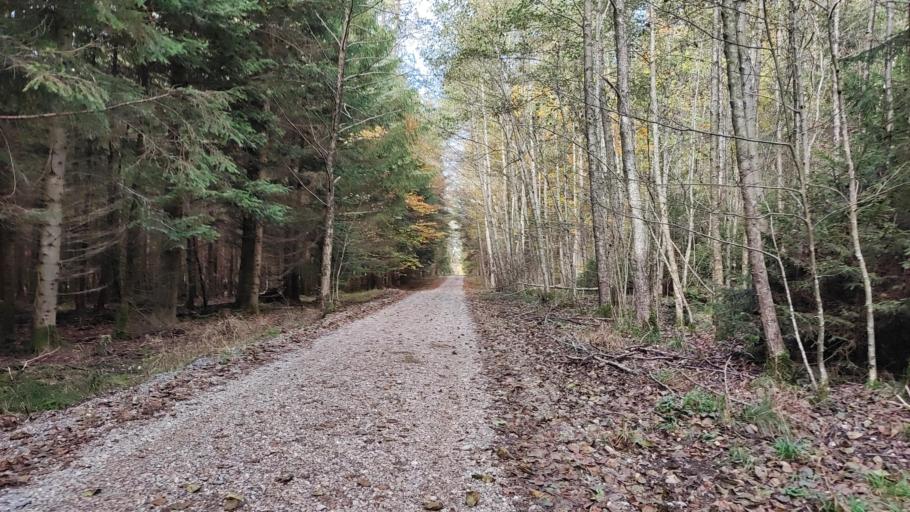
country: DE
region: Bavaria
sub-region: Swabia
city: Burtenbach
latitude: 48.3327
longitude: 10.4967
